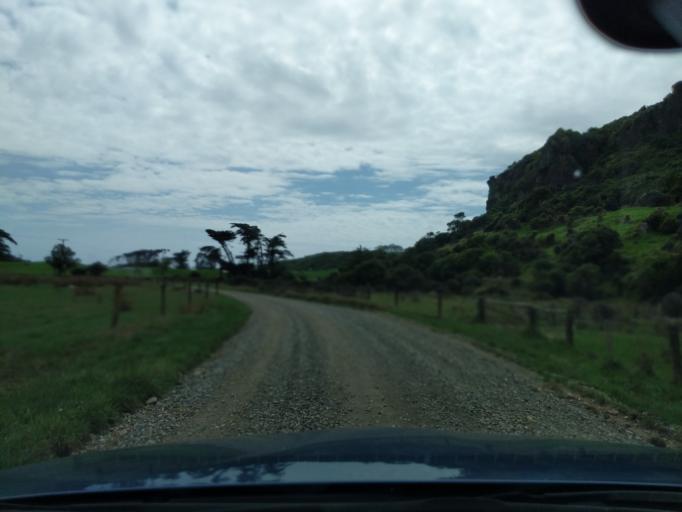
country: NZ
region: Tasman
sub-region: Tasman District
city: Takaka
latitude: -40.6470
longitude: 172.4380
